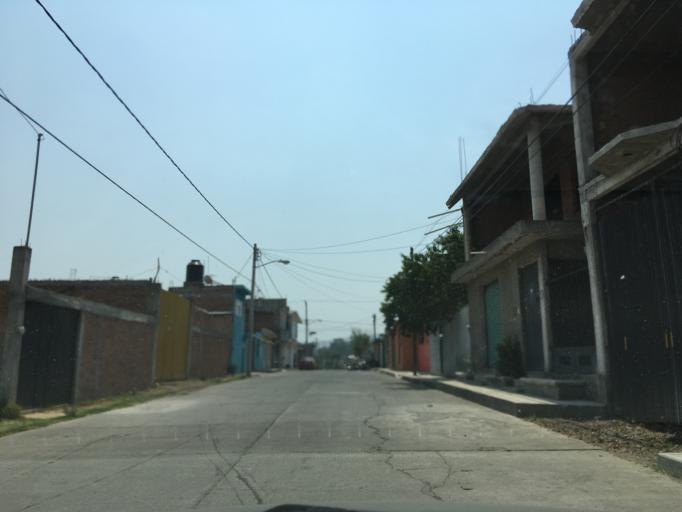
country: MX
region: Michoacan
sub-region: Morelia
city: Morelos
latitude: 19.6457
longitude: -101.2355
